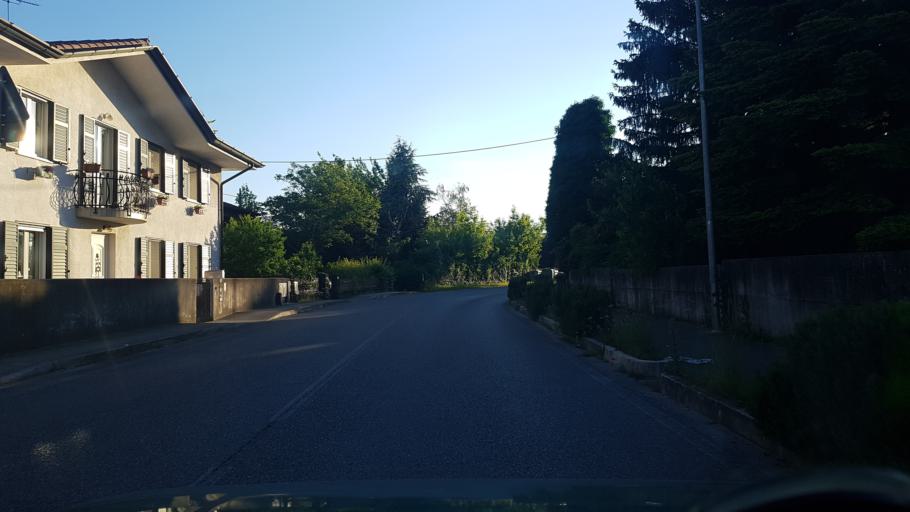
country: IT
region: Friuli Venezia Giulia
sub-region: Provincia di Udine
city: Aiello del Friuli
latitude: 45.8750
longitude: 13.3567
